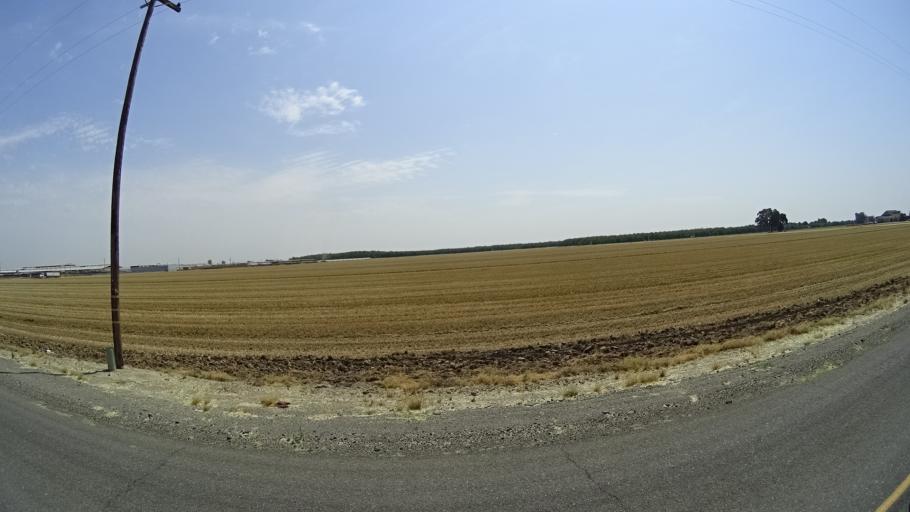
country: US
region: California
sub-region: Kings County
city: Armona
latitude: 36.3363
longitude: -119.7449
